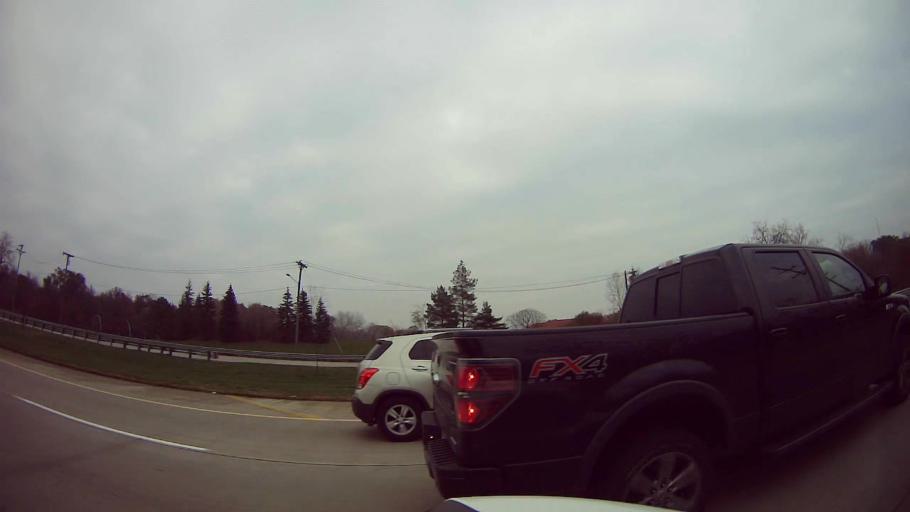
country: US
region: Michigan
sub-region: Wayne County
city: Dearborn Heights
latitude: 42.3450
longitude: -83.2739
